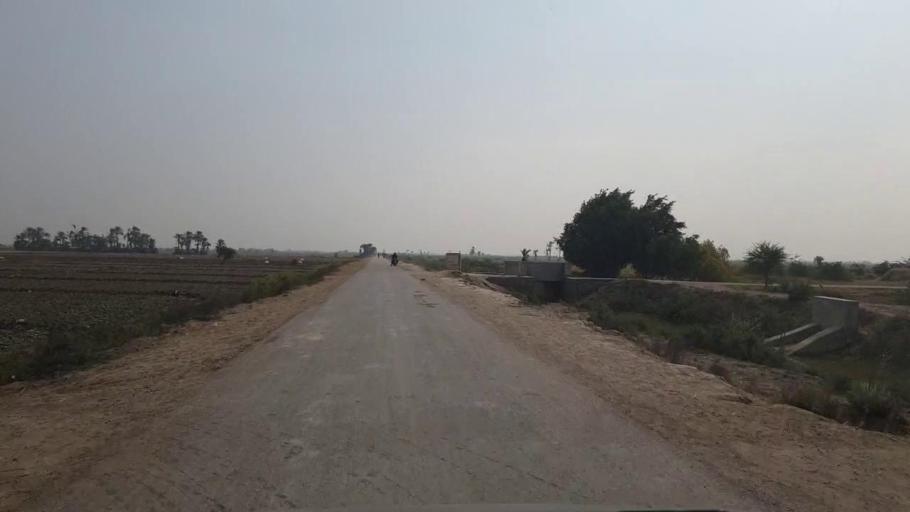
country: PK
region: Sindh
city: Tando Muhammad Khan
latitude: 25.1045
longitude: 68.3703
